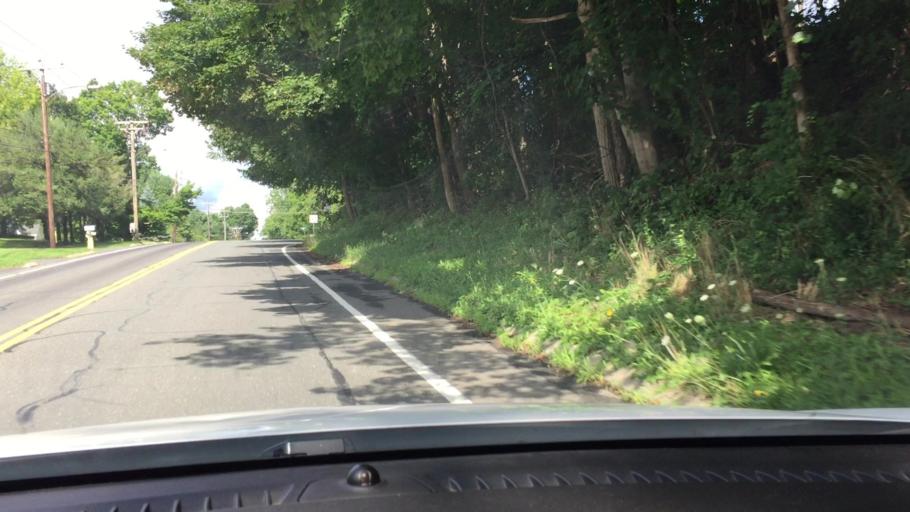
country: US
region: Massachusetts
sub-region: Berkshire County
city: Pittsfield
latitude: 42.4527
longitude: -73.2827
